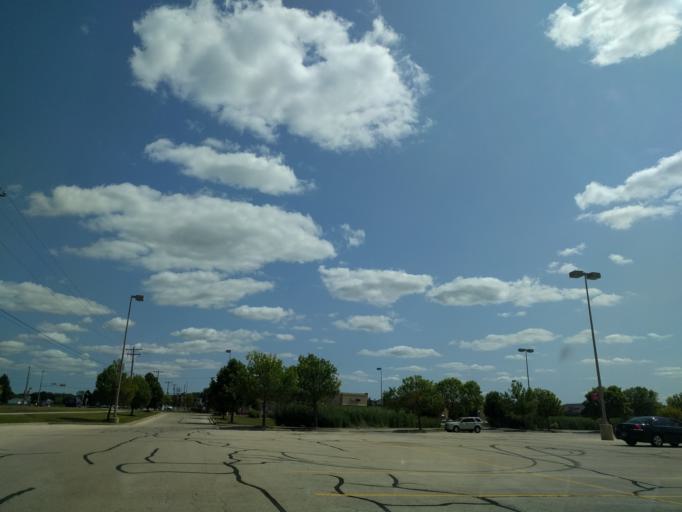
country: US
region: Wisconsin
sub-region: Brown County
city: Allouez
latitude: 44.4661
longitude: -87.9849
